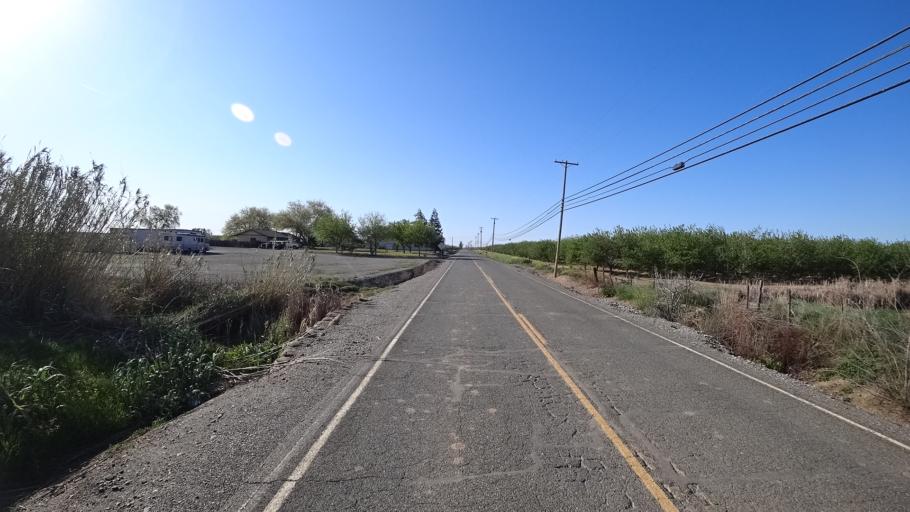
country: US
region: California
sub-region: Glenn County
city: Orland
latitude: 39.7814
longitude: -122.1041
